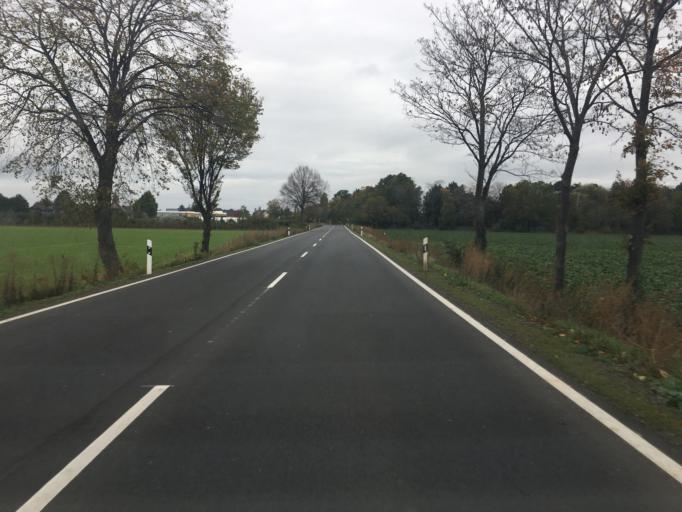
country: DE
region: North Rhine-Westphalia
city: Zulpich
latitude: 50.6739
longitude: 6.7045
